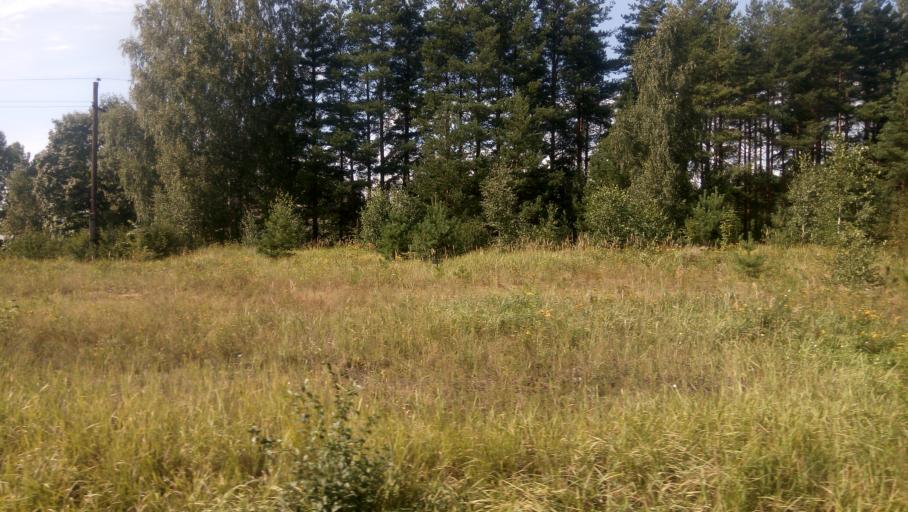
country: RU
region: Moskovskaya
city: Vereya
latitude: 55.8462
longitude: 39.0683
